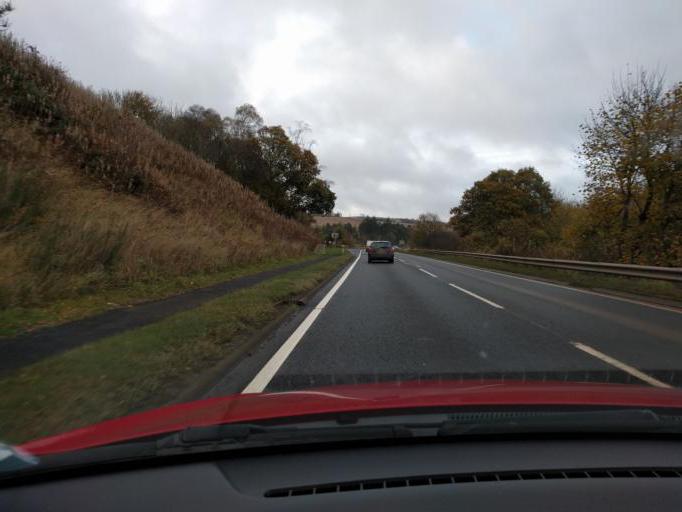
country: GB
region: Scotland
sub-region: The Scottish Borders
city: Duns
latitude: 55.8826
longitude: -2.2993
